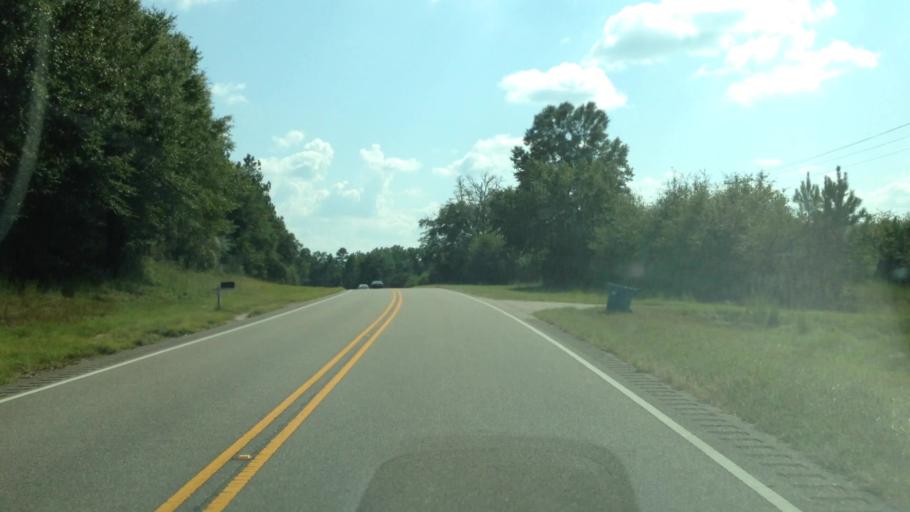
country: US
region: Alabama
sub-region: Covington County
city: Andalusia
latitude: 31.0764
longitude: -86.5752
